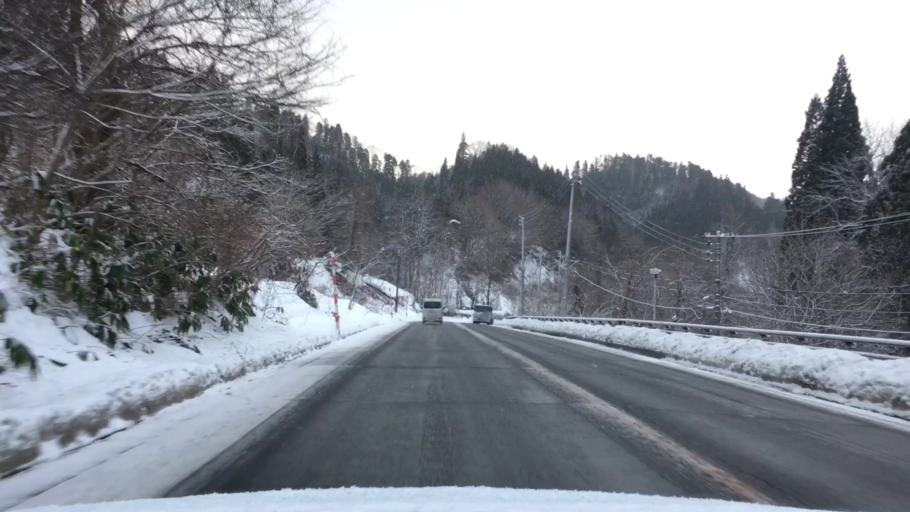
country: JP
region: Akita
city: Odate
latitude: 40.4310
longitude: 140.6367
